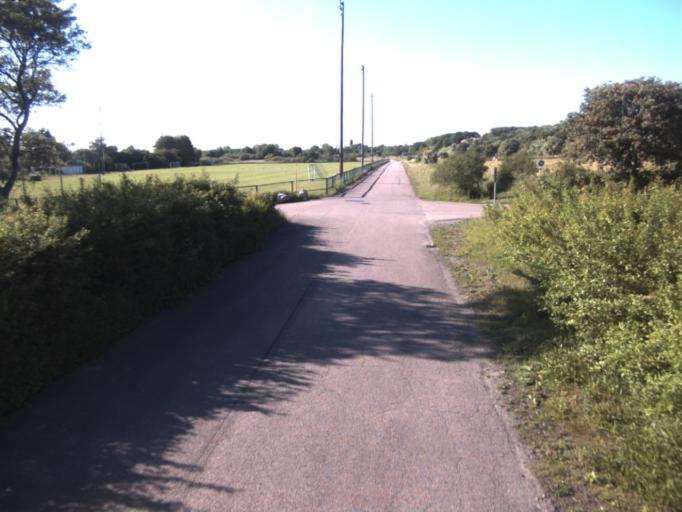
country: SE
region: Skane
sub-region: Helsingborg
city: Rydeback
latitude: 55.9818
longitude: 12.7578
